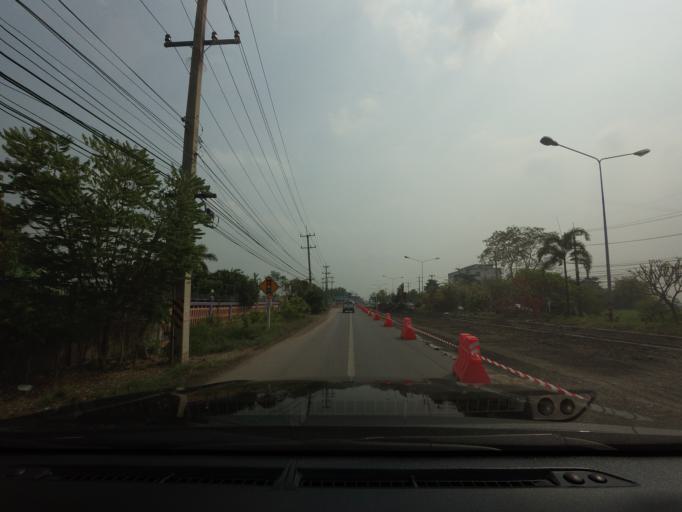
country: TH
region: Nakhon Nayok
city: Nakhon Nayok
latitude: 14.1911
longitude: 101.2267
